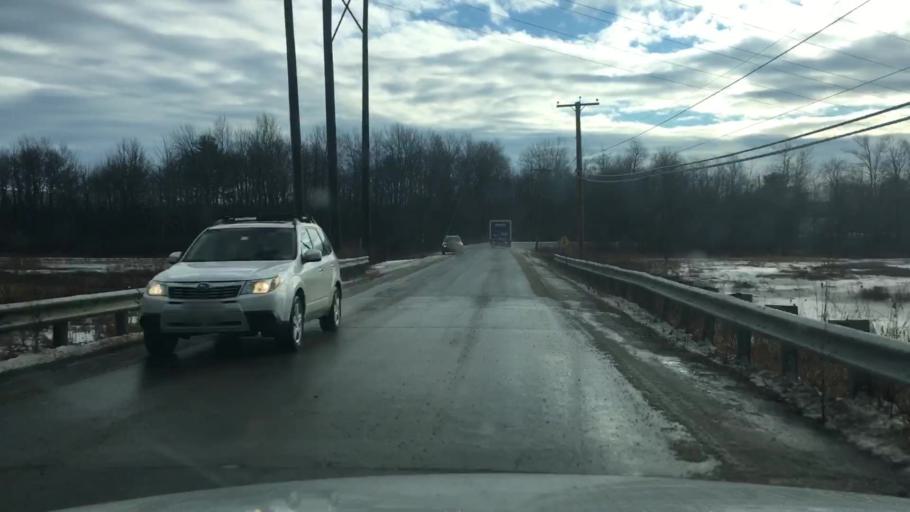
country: US
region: Maine
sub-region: Penobscot County
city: Brewer
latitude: 44.7297
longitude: -68.7568
